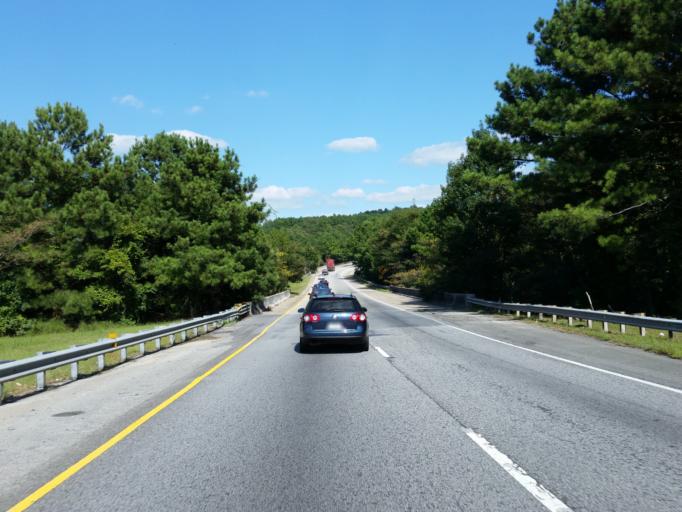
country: US
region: Georgia
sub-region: Clayton County
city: Conley
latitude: 33.6701
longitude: -84.3329
